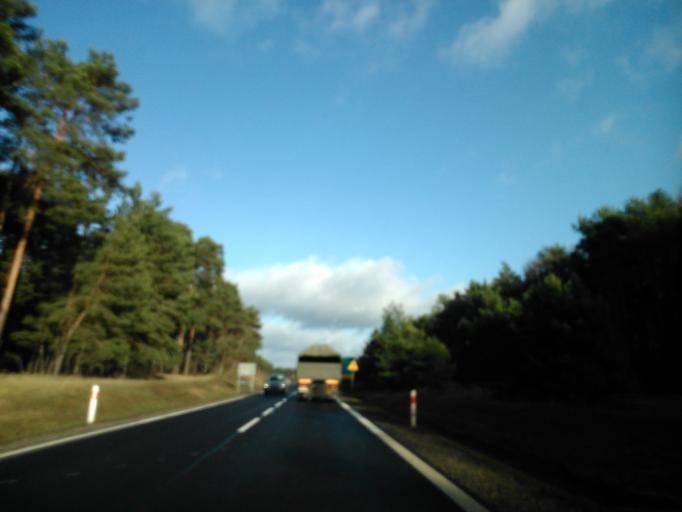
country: PL
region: Kujawsko-Pomorskie
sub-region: Powiat torunski
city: Wielka Nieszawka
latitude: 52.9663
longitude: 18.5379
